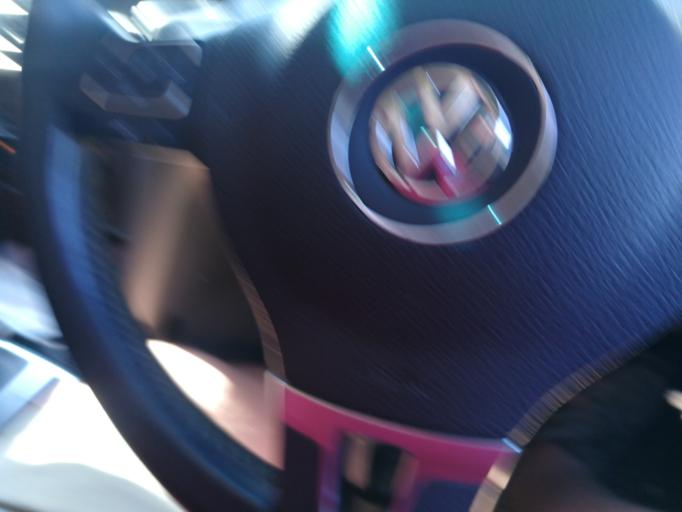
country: ZA
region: Limpopo
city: Thulamahashi
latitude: -24.9925
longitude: 31.5175
